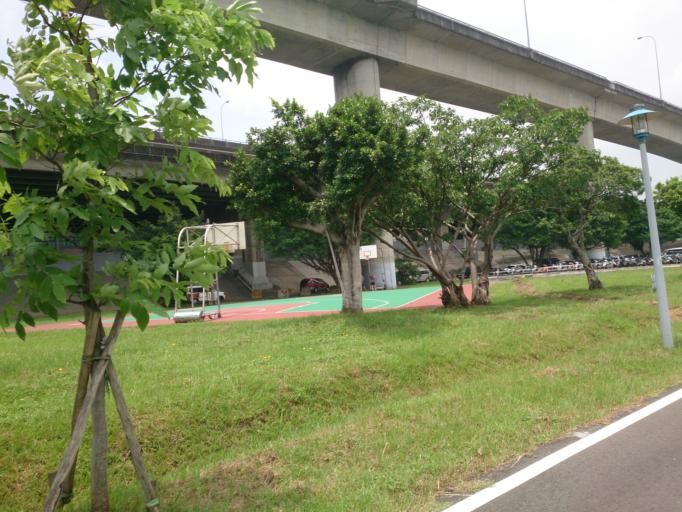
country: TW
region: Taipei
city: Taipei
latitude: 25.0775
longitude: 121.5203
